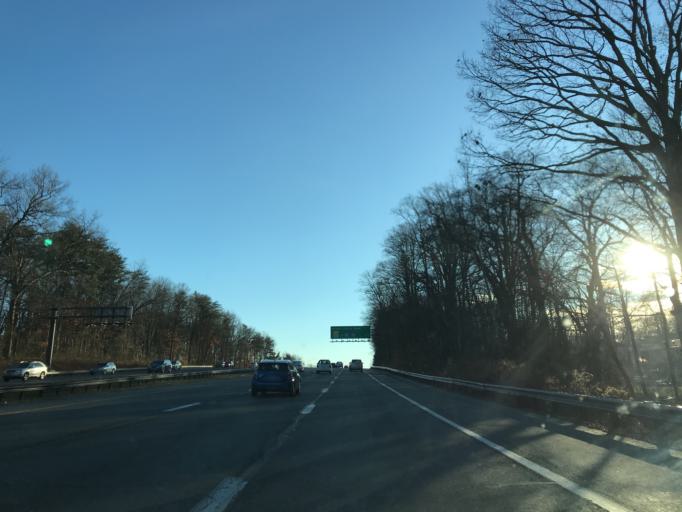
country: US
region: Maryland
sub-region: Montgomery County
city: Burtonsville
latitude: 39.0996
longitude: -76.9359
